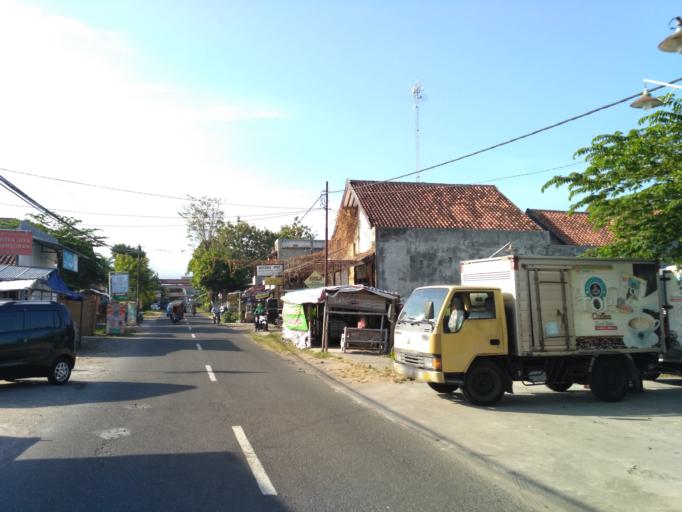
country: ID
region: Daerah Istimewa Yogyakarta
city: Depok
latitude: -7.7754
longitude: 110.4236
